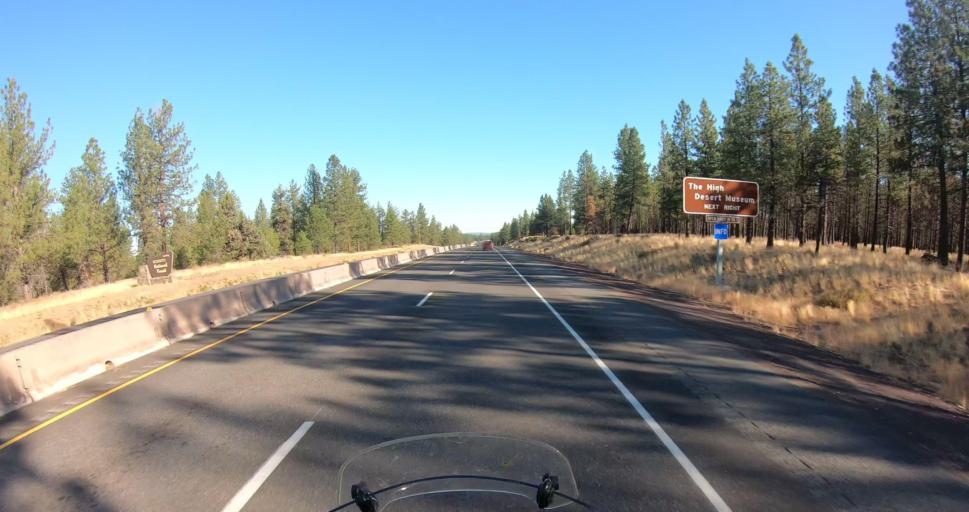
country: US
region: Oregon
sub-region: Deschutes County
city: Deschutes River Woods
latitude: 43.9632
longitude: -121.3474
